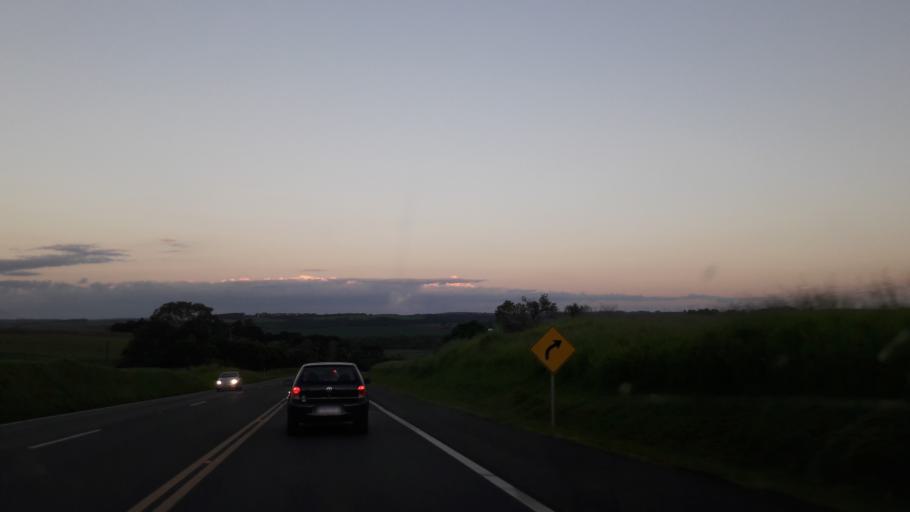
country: BR
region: Parana
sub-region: Palmeira
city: Palmeira
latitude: -25.4241
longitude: -50.1091
